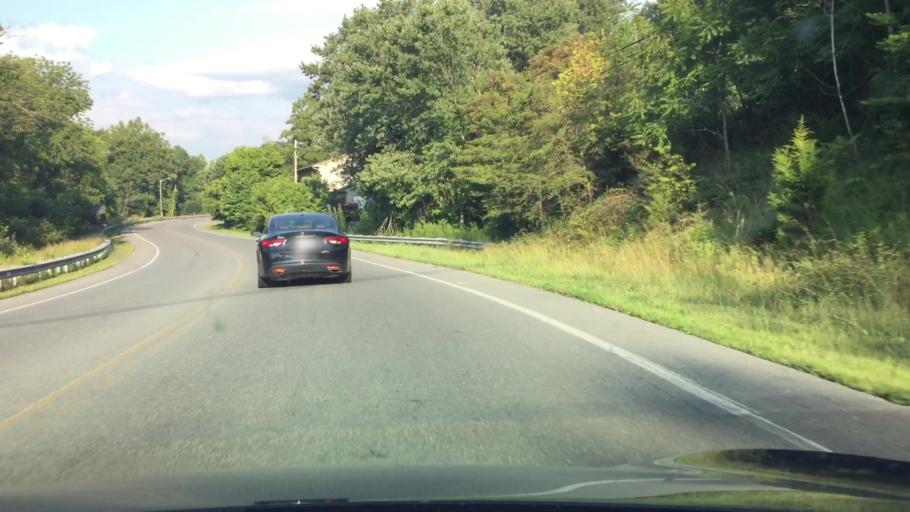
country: US
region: Virginia
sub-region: City of Radford
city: Radford
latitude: 37.1183
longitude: -80.5488
